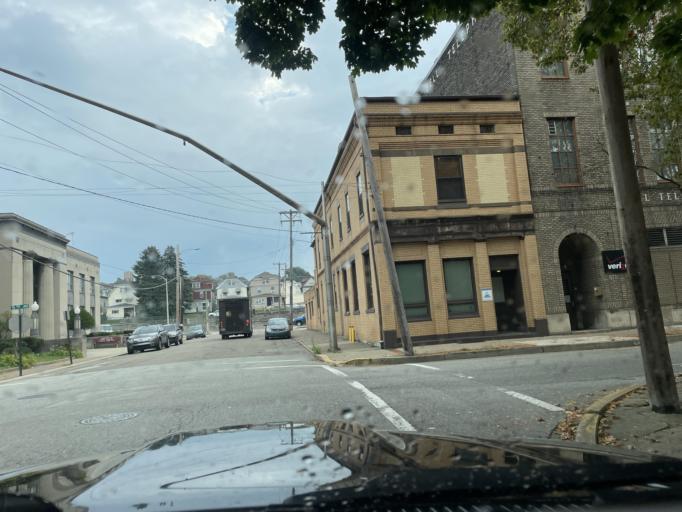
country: US
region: Pennsylvania
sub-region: Westmoreland County
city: New Kensington
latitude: 40.5682
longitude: -79.7660
